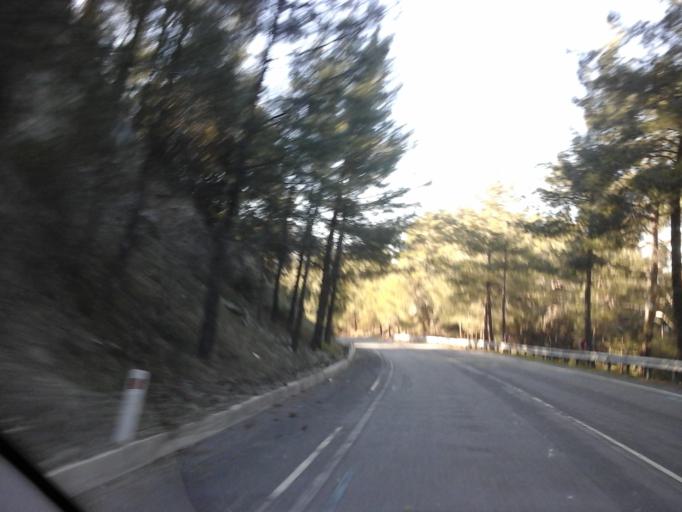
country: CY
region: Limassol
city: Kyperounta
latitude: 34.9442
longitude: 32.9282
